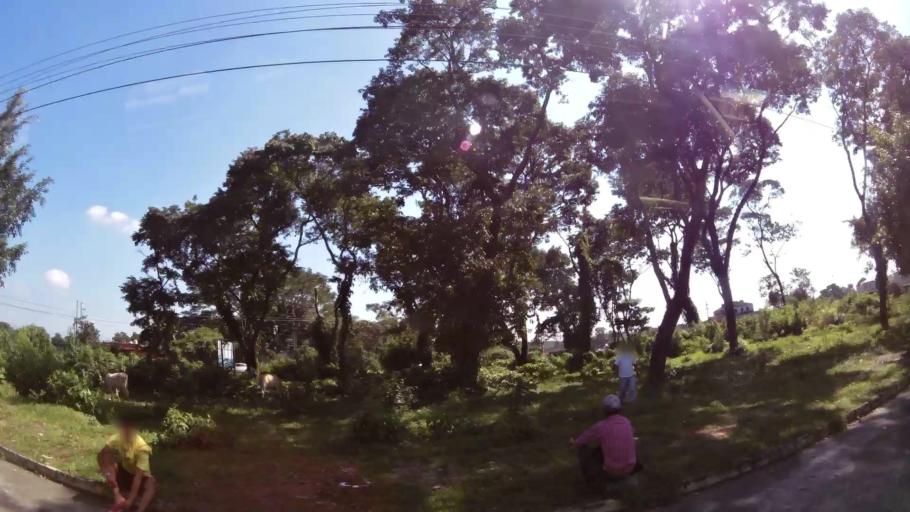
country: GT
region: Suchitepeque
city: Mazatenango
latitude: 14.5473
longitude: -91.5053
